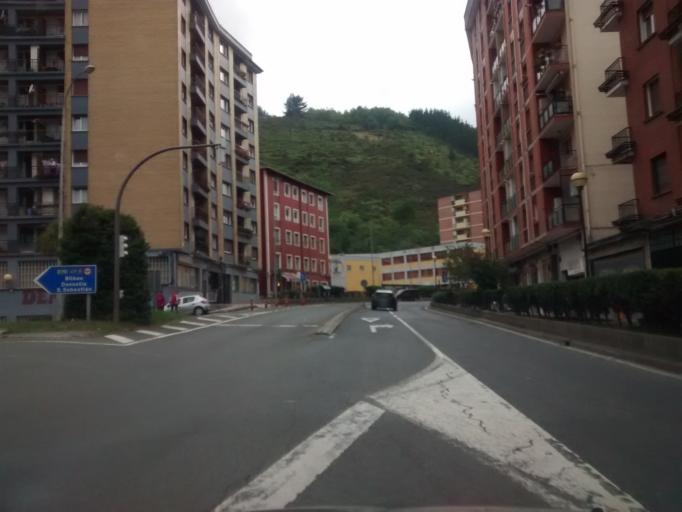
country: ES
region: Basque Country
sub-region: Bizkaia
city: Ermua
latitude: 43.1791
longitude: -2.4967
